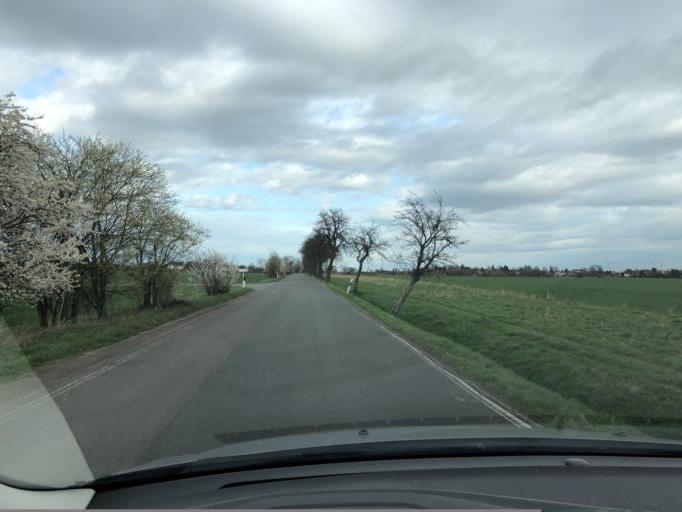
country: DE
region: Saxony
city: Markranstadt
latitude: 51.2766
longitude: 12.2164
